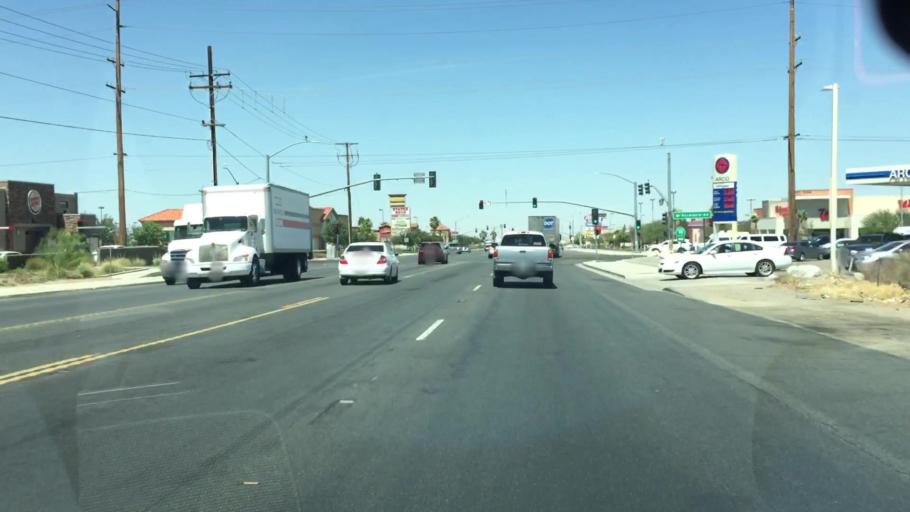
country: US
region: California
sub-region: San Bernardino County
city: Mountain View Acres
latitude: 34.5060
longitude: -117.3995
